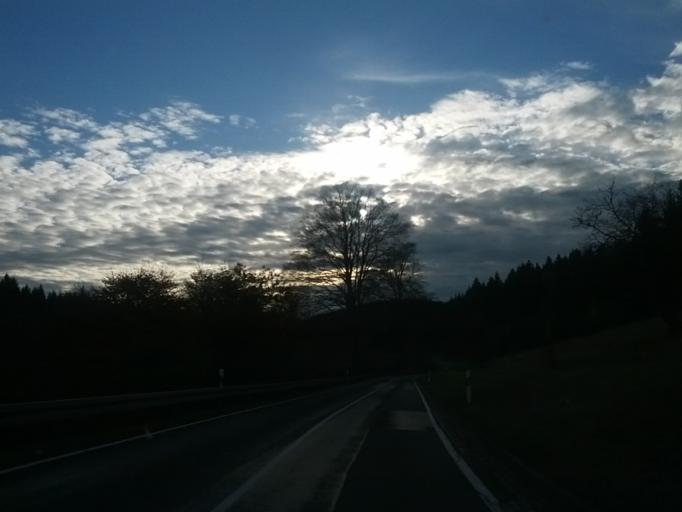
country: DE
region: Thuringia
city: Brotterode
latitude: 50.8364
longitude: 10.4684
